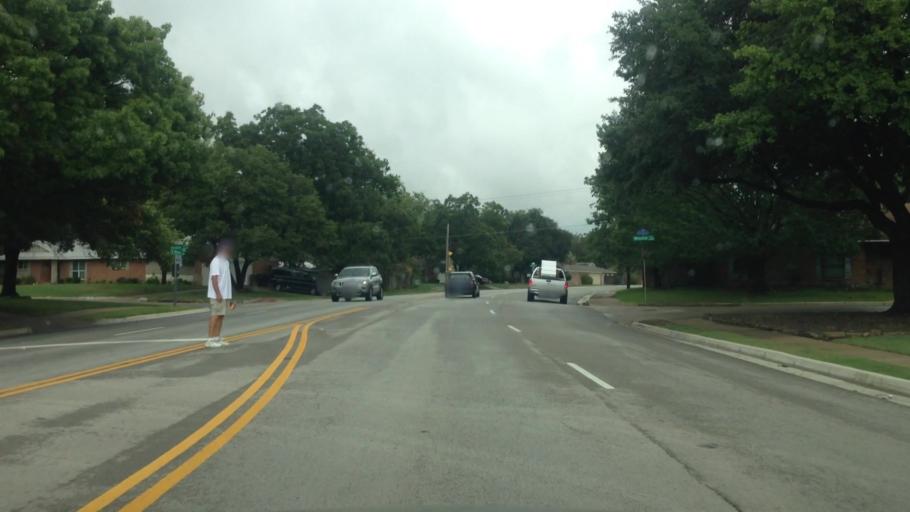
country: US
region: Texas
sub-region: Tarrant County
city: Edgecliff Village
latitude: 32.6586
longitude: -97.3981
